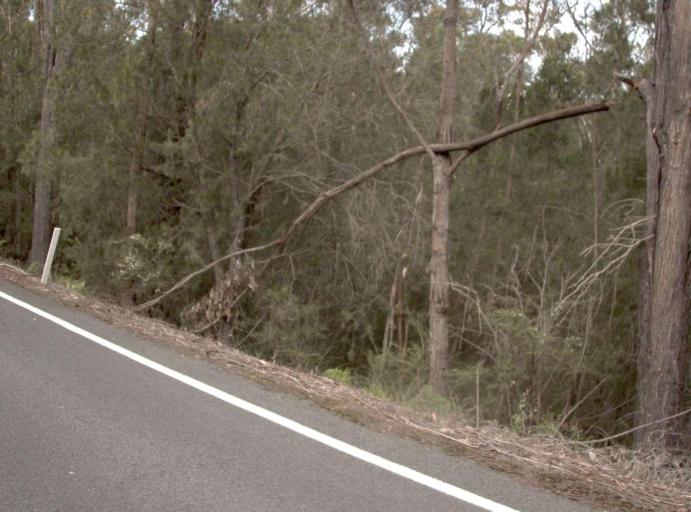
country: AU
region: New South Wales
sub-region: Bega Valley
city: Eden
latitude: -37.4953
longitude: 149.5483
